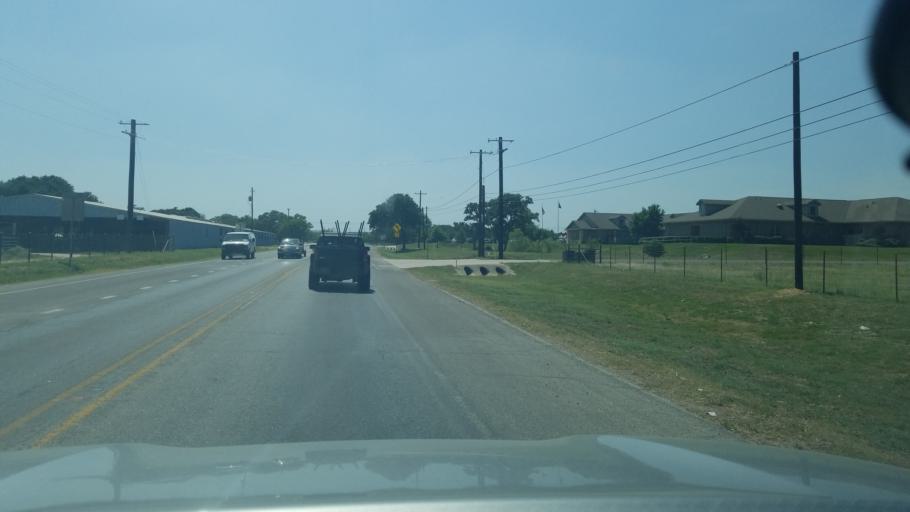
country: US
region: Texas
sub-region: Kendall County
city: Boerne
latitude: 29.7891
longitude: -98.7082
